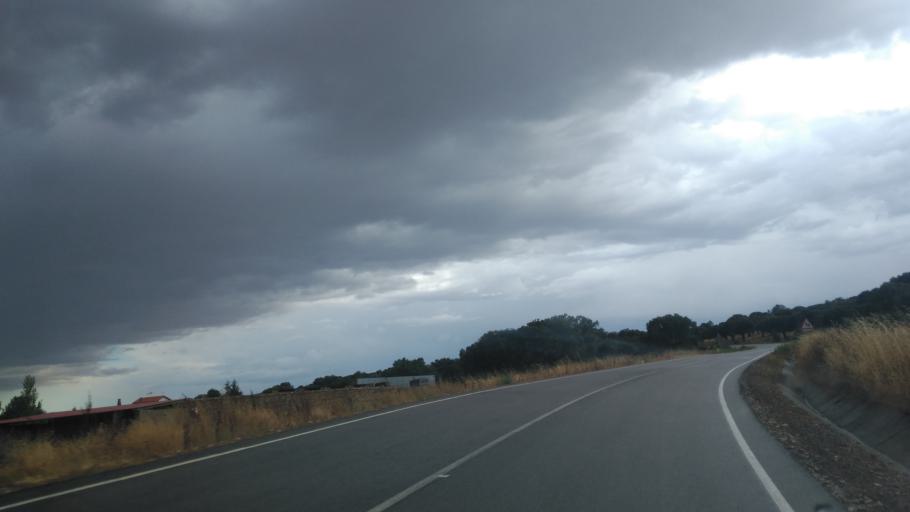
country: ES
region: Castille and Leon
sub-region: Provincia de Salamanca
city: Aldeanueva de la Sierra
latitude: 40.6071
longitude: -6.1364
